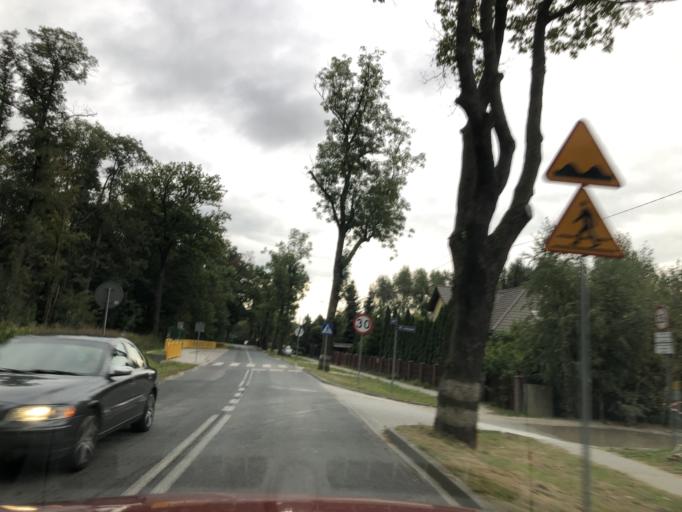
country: PL
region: Lower Silesian Voivodeship
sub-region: Powiat wroclawski
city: Dlugoleka
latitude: 51.1860
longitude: 17.1859
